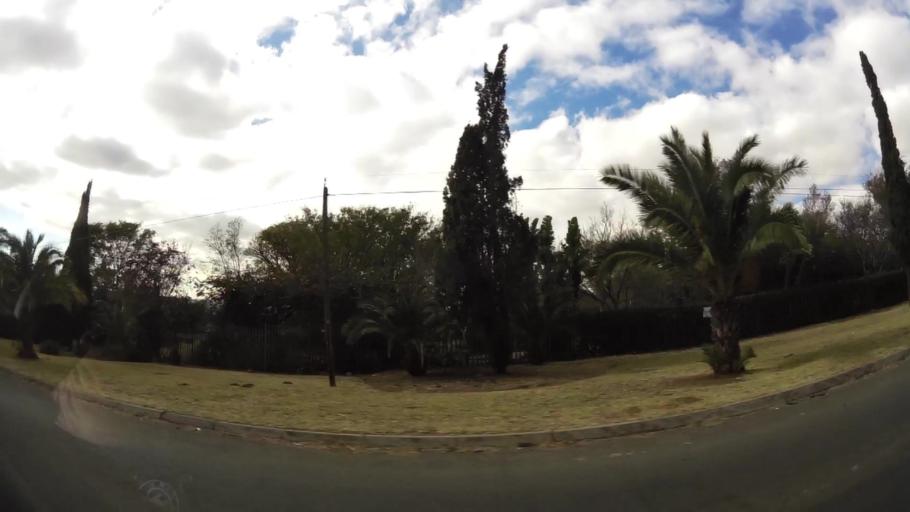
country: ZA
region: Gauteng
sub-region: West Rand District Municipality
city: Muldersdriseloop
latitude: -26.0809
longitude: 27.8562
